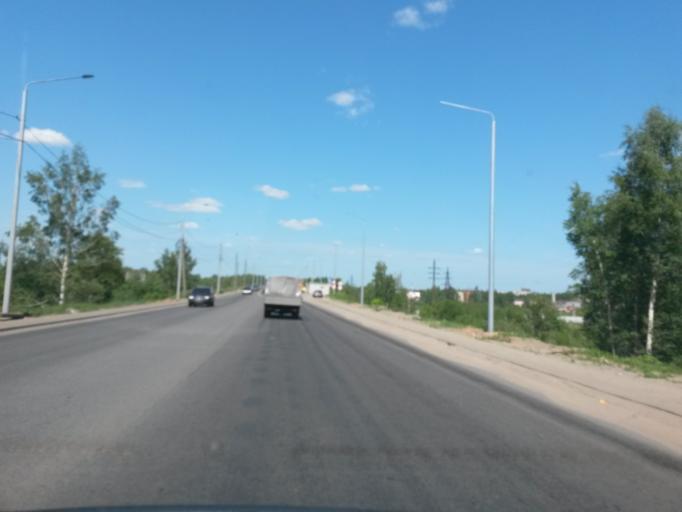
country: RU
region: Jaroslavl
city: Yaroslavl
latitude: 57.5865
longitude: 39.8210
